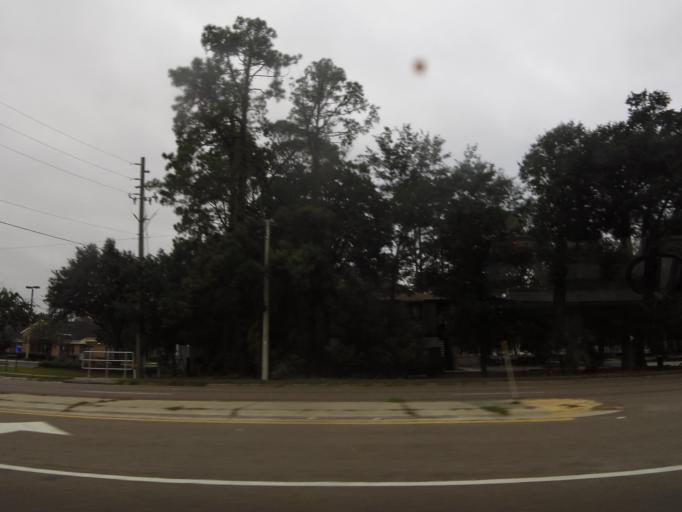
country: US
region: Florida
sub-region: Clay County
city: Bellair-Meadowbrook Terrace
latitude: 30.2480
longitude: -81.7759
